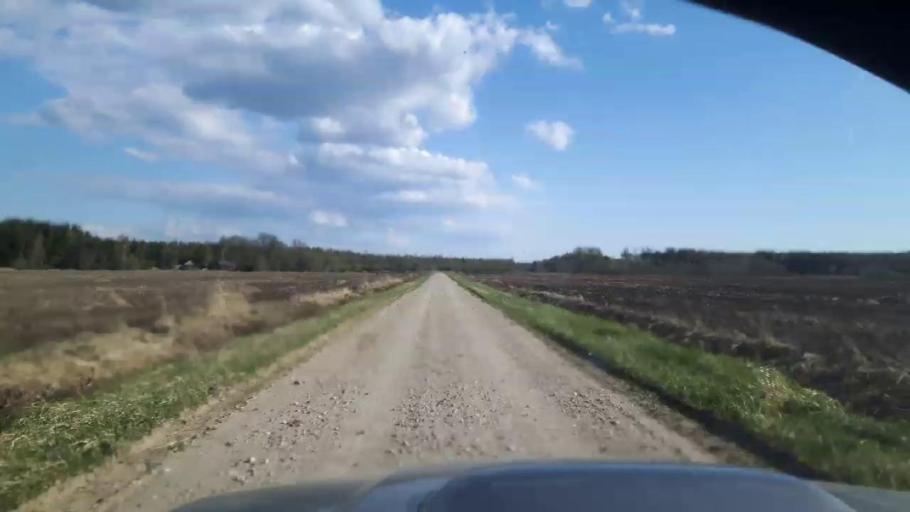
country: EE
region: Paernumaa
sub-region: Tootsi vald
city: Tootsi
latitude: 58.4159
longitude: 24.8532
